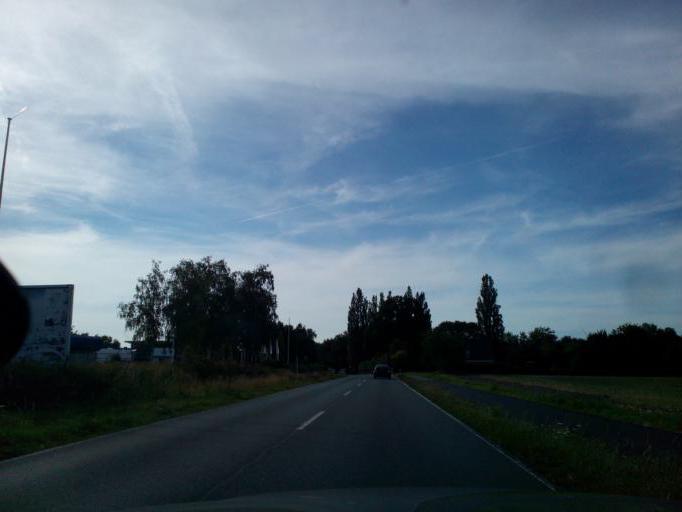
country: DE
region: North Rhine-Westphalia
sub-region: Regierungsbezirk Munster
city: Muenster
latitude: 51.9512
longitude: 7.5554
